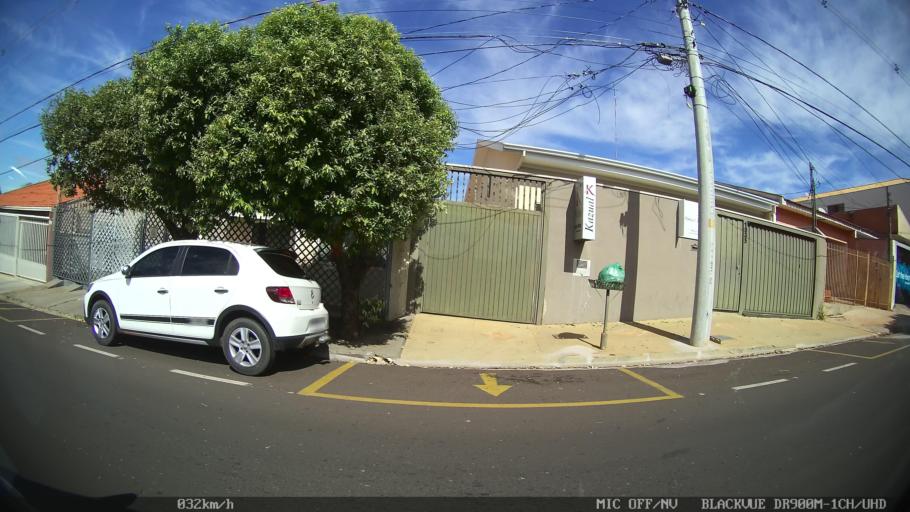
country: BR
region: Sao Paulo
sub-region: Sao Jose Do Rio Preto
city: Sao Jose do Rio Preto
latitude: -20.8442
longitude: -49.3651
